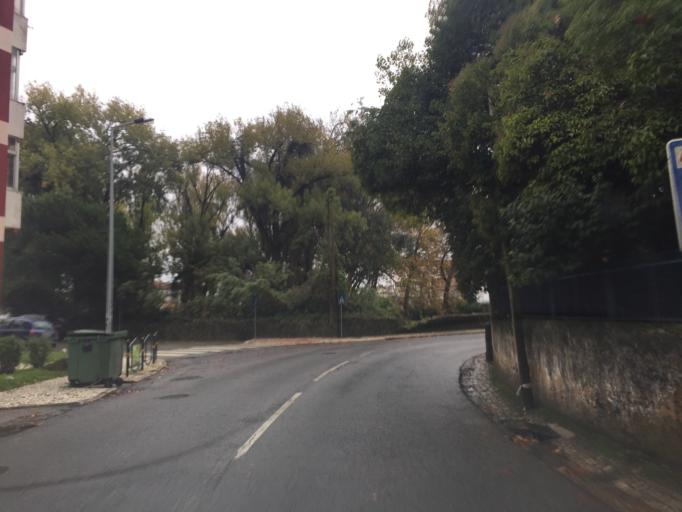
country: PT
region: Lisbon
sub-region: Sintra
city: Rio de Mouro
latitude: 38.7933
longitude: -9.3467
